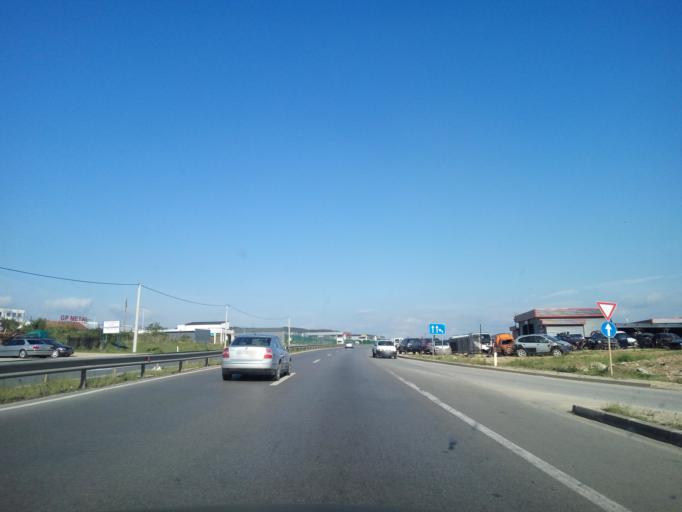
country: XK
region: Pristina
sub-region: Komuna e Drenasit
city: Glogovac
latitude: 42.6024
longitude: 20.9548
